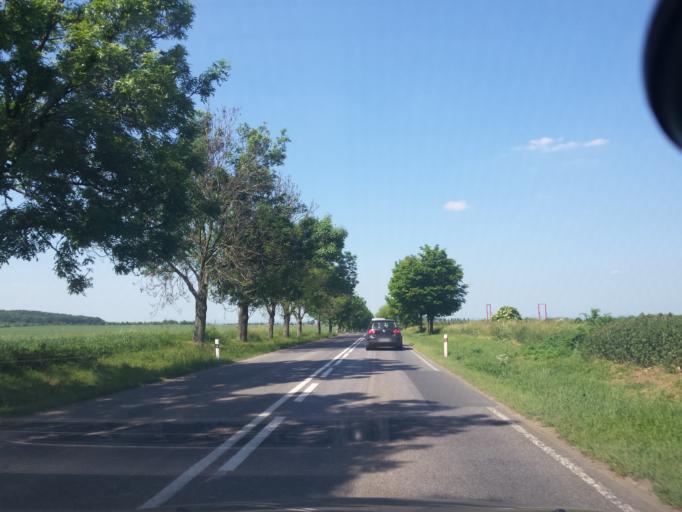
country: CZ
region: Central Bohemia
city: Velke Prilepy
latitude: 50.1702
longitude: 14.3168
